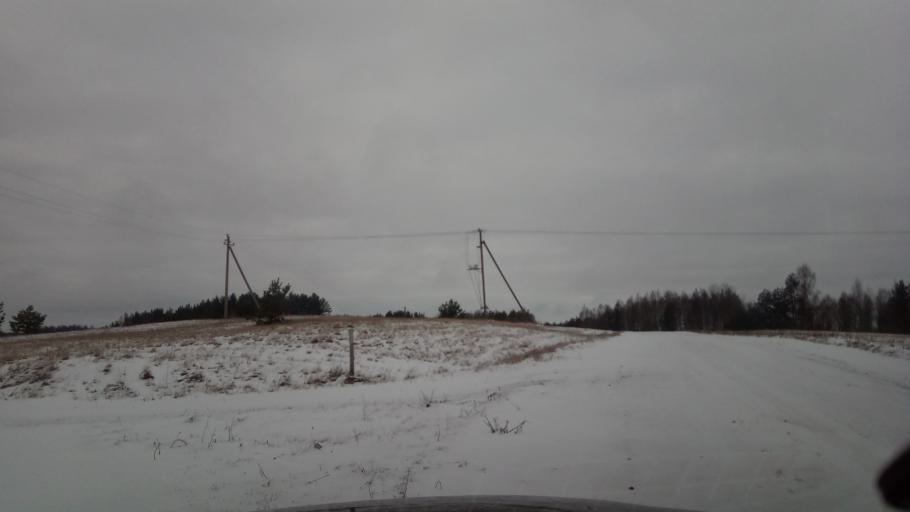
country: LT
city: Zarasai
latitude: 55.6888
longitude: 26.0983
